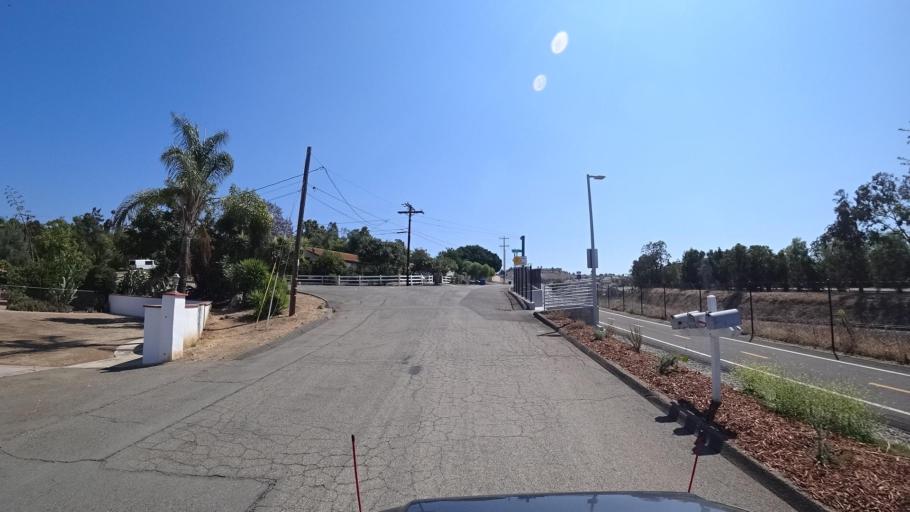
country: US
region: California
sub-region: San Diego County
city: Lake San Marcos
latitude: 33.1650
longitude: -117.2010
